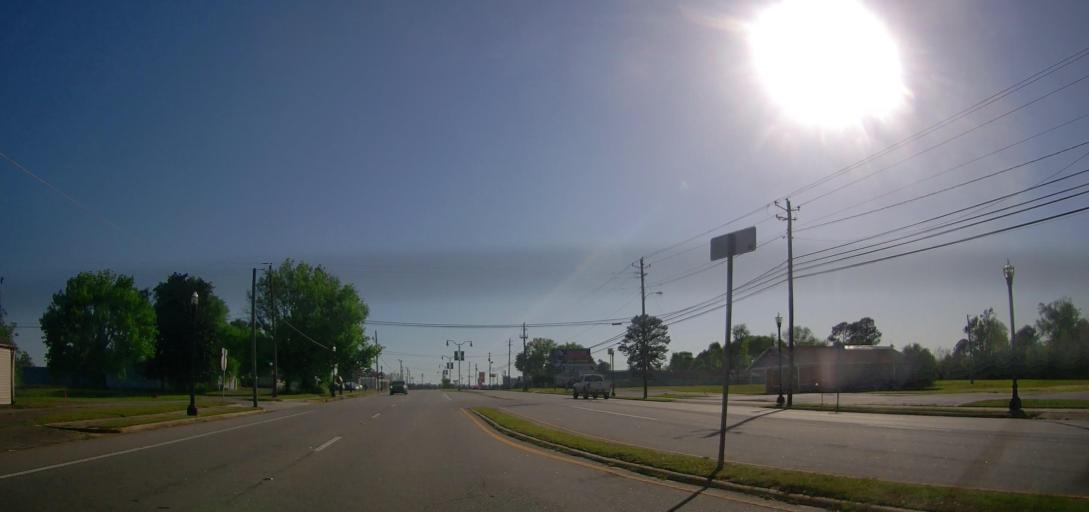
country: US
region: Georgia
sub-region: Houston County
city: Perry
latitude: 32.4487
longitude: -83.7476
